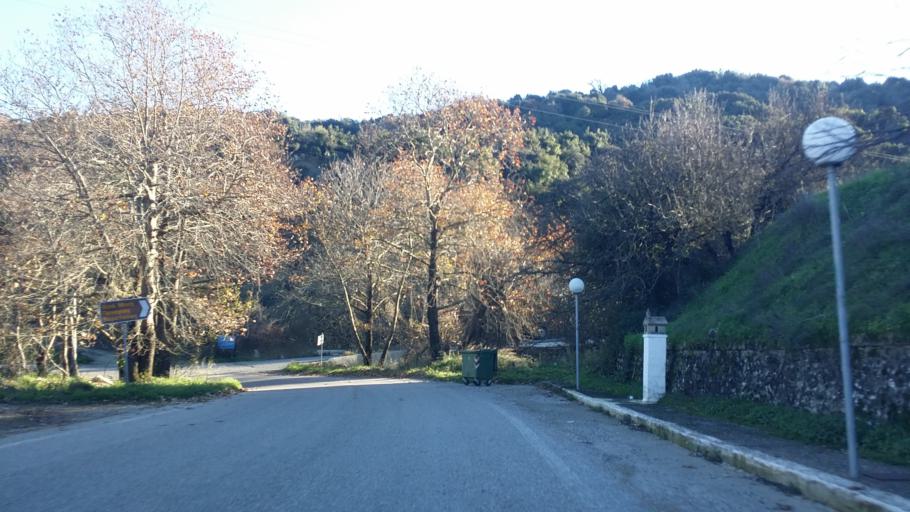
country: GR
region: West Greece
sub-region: Nomos Aitolias kai Akarnanias
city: Sardinia
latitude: 38.8667
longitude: 21.2881
